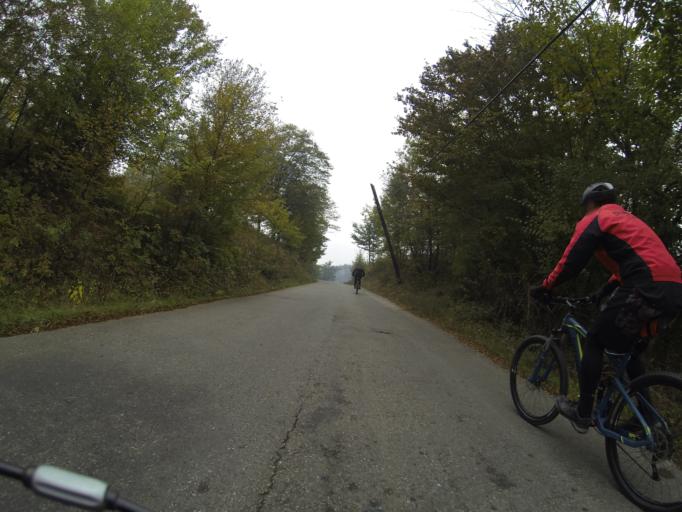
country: RO
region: Gorj
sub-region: Comuna Tismana
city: Pocruia
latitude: 45.0419
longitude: 22.9136
